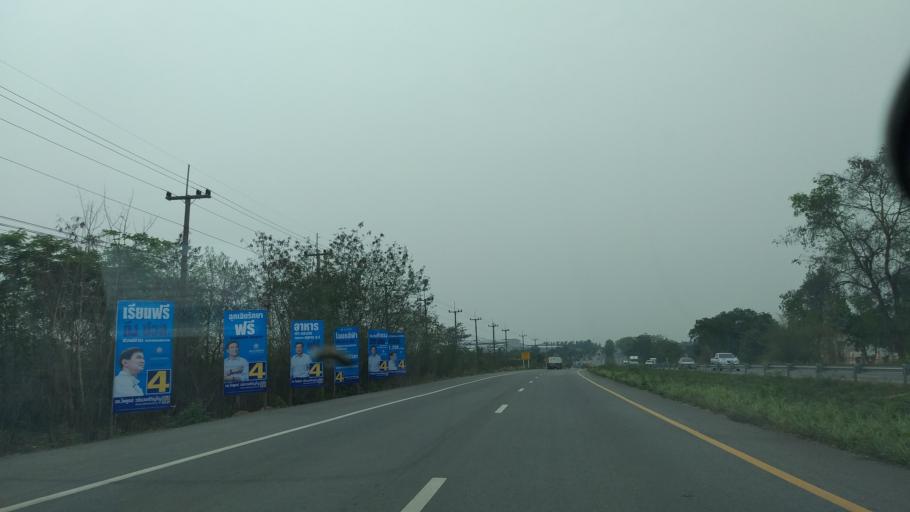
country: TH
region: Chachoengsao
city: Plaeng Yao
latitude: 13.4960
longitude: 101.2727
